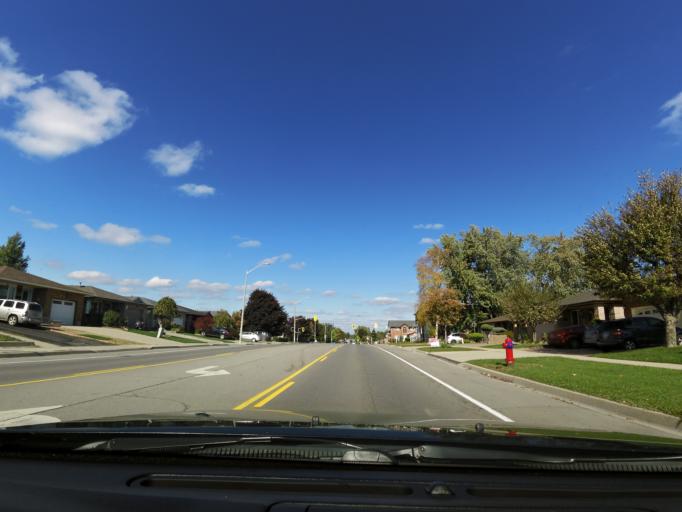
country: CA
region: Ontario
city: Ancaster
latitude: 43.2227
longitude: -79.9166
